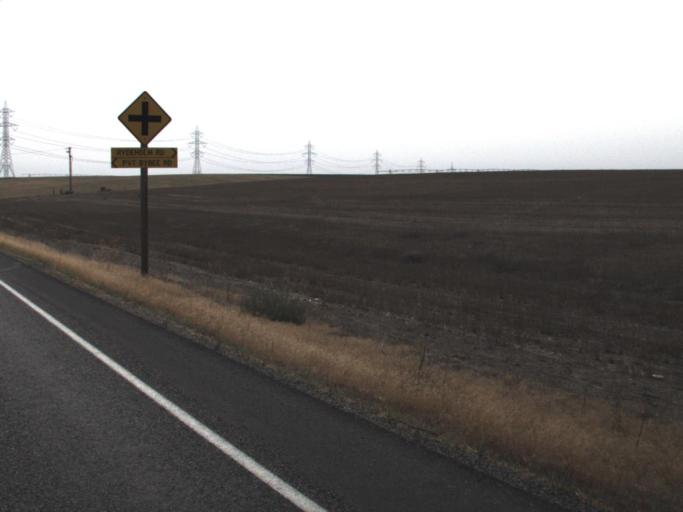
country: US
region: Washington
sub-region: Benton County
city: Prosser
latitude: 46.0900
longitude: -119.6020
